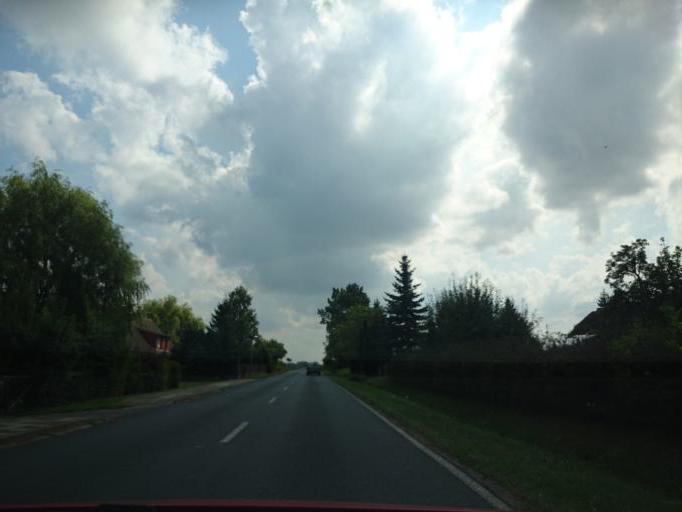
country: DE
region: Mecklenburg-Vorpommern
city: Velgast
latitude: 54.3257
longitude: 12.7950
